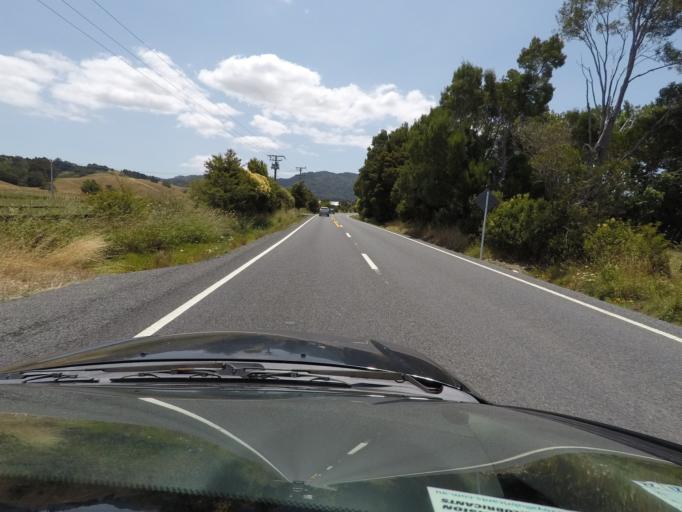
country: NZ
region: Auckland
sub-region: Auckland
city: Warkworth
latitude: -36.3317
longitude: 174.7330
